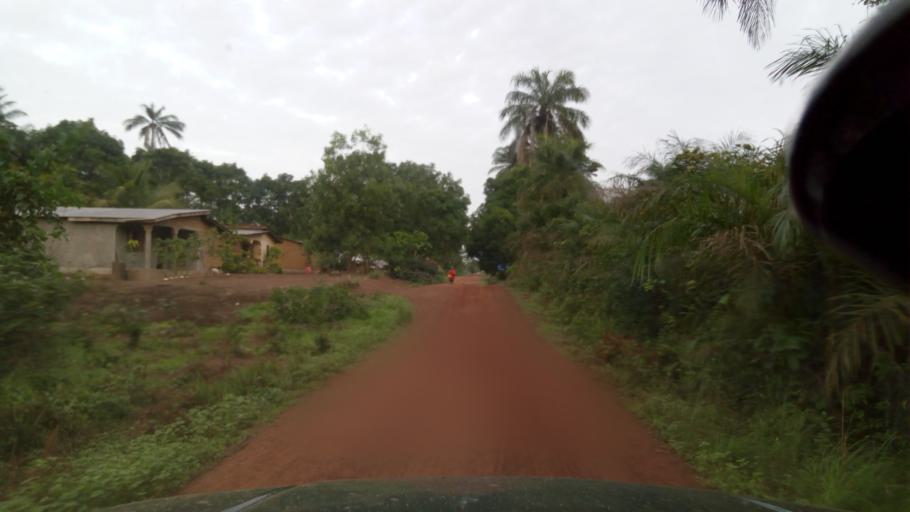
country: SL
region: Northern Province
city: Port Loko
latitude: 8.7164
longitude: -12.8035
